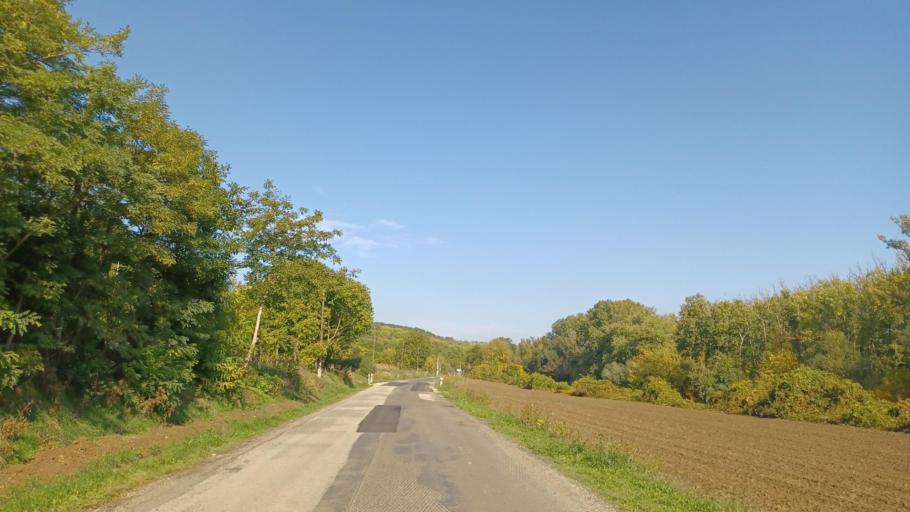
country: HU
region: Tolna
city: Nagydorog
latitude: 46.5691
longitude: 18.5917
